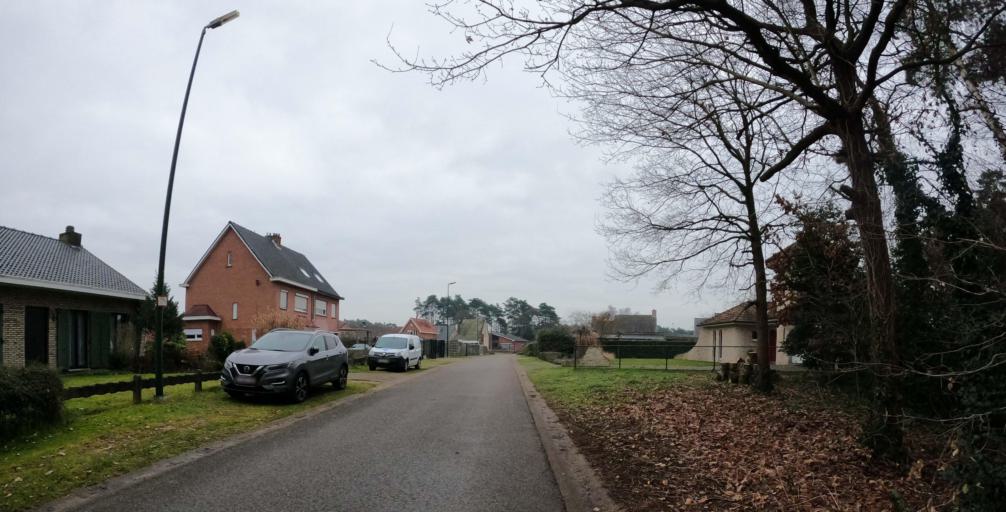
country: BE
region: Flanders
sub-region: Provincie Antwerpen
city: Vorselaar
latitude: 51.2023
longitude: 4.7571
